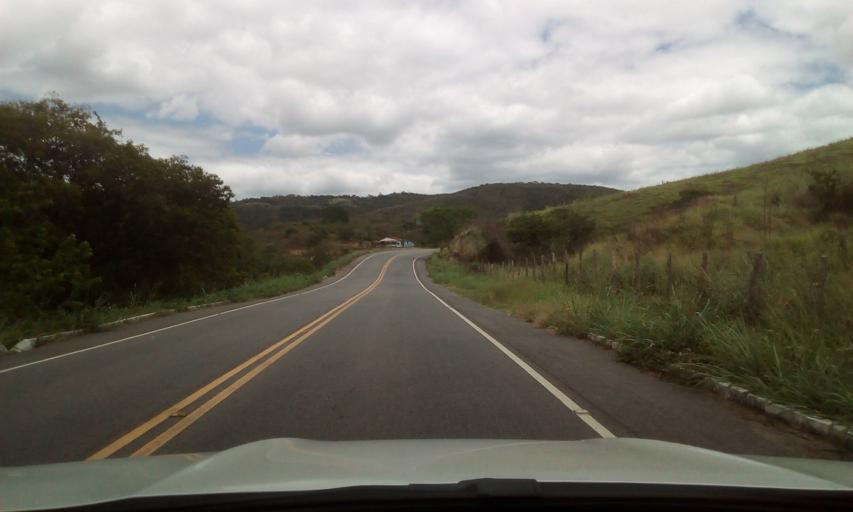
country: BR
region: Paraiba
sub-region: Serra Redonda
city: Alagoa Grande
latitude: -7.1538
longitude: -35.6097
